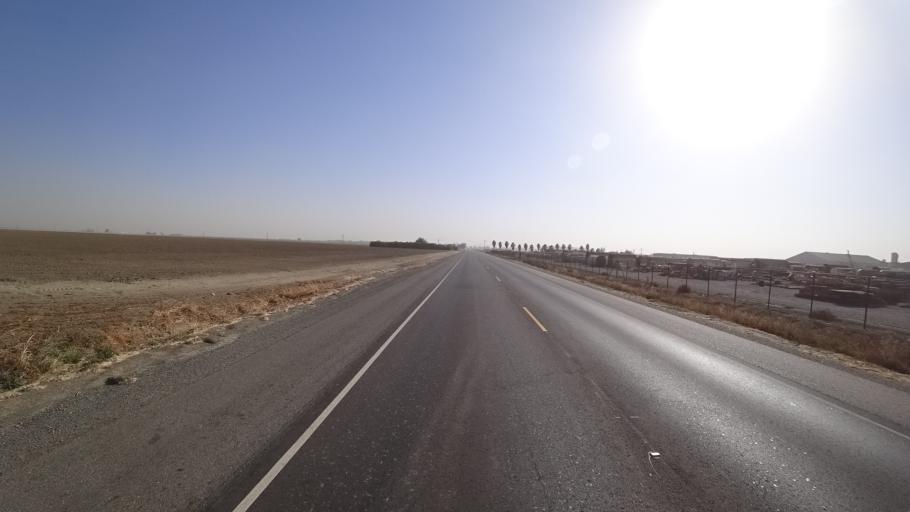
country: US
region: California
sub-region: Yolo County
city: Woodland
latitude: 38.7523
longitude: -121.7293
